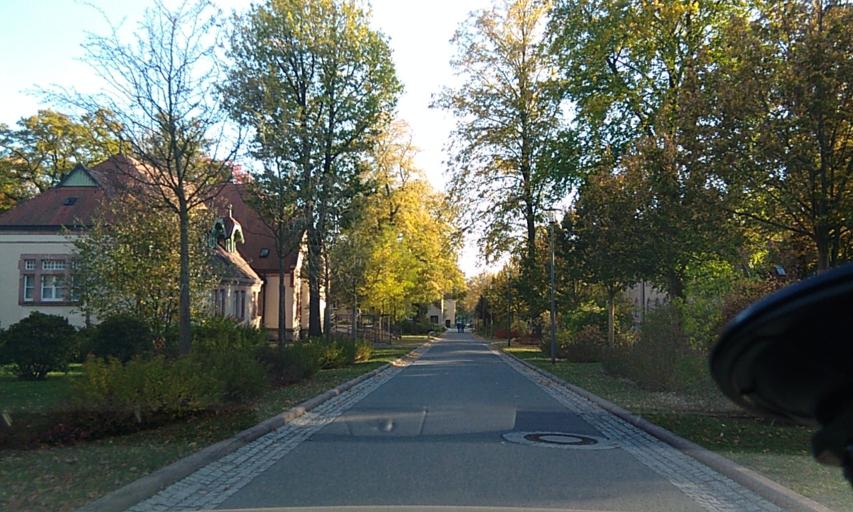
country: DE
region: Saxony
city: Wittgensdorf
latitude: 50.8446
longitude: 12.8756
